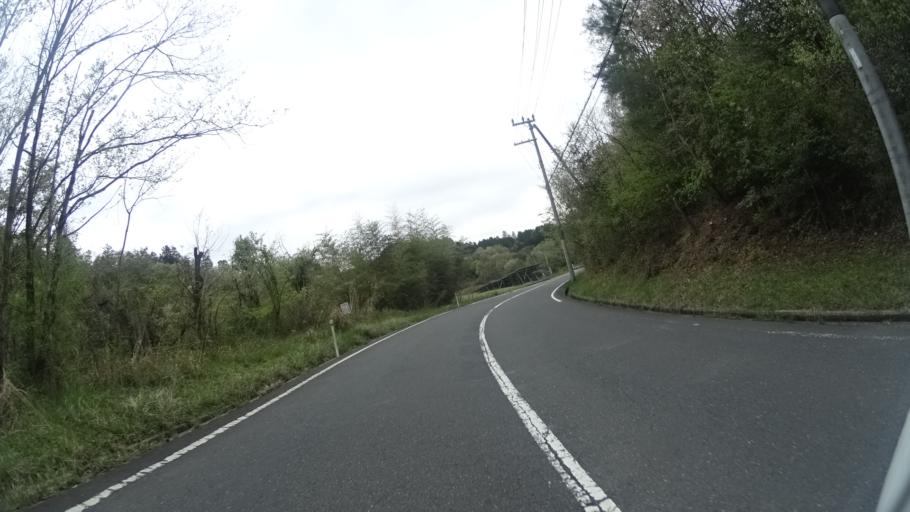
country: JP
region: Kyoto
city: Kameoka
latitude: 35.1829
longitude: 135.4529
